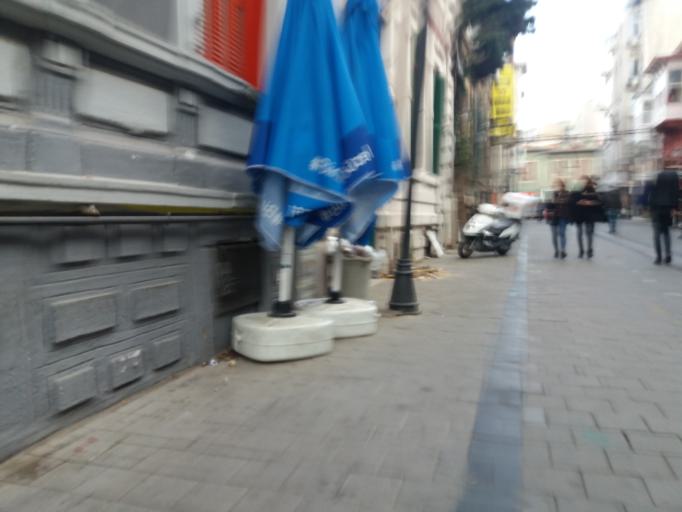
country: TR
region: Izmir
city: Izmir
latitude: 38.4373
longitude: 27.1424
